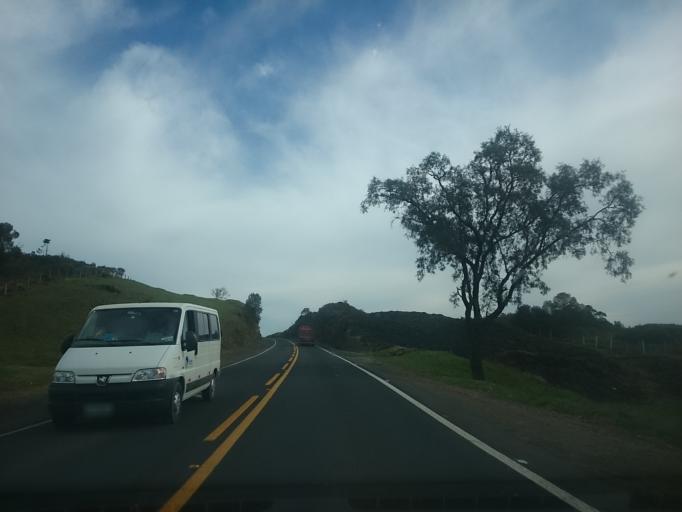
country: BR
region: Rio Grande do Sul
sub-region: Vacaria
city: Estrela
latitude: -28.1050
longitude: -50.6145
